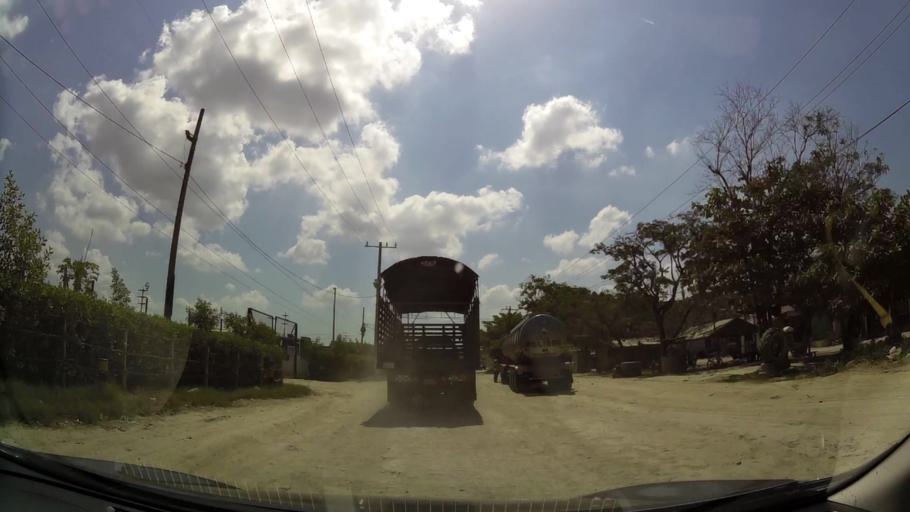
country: CO
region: Bolivar
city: Cartagena
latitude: 10.3455
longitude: -75.4867
